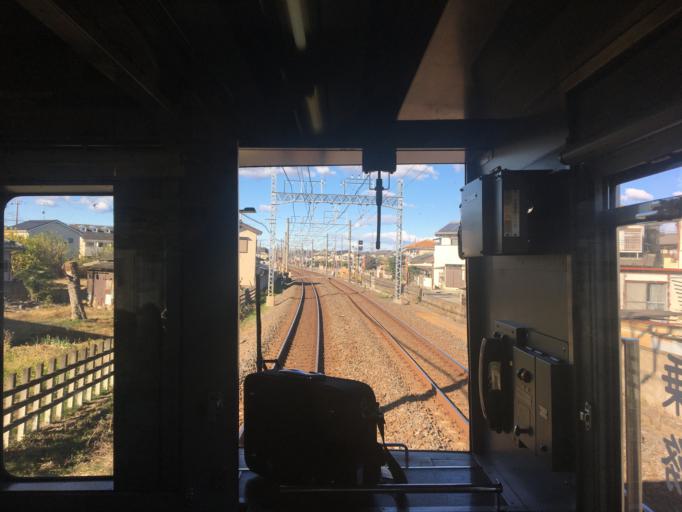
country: JP
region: Saitama
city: Fukiage-fujimi
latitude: 36.0415
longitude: 139.3922
